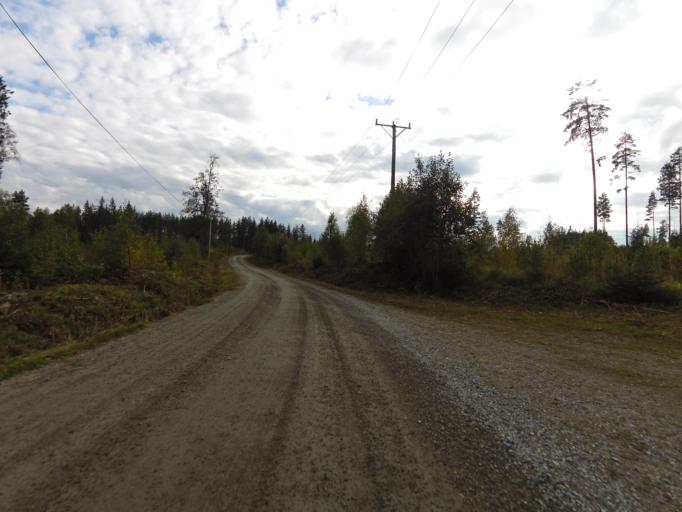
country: SE
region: Gaevleborg
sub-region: Sandvikens Kommun
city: Sandviken
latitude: 60.7197
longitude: 16.8120
